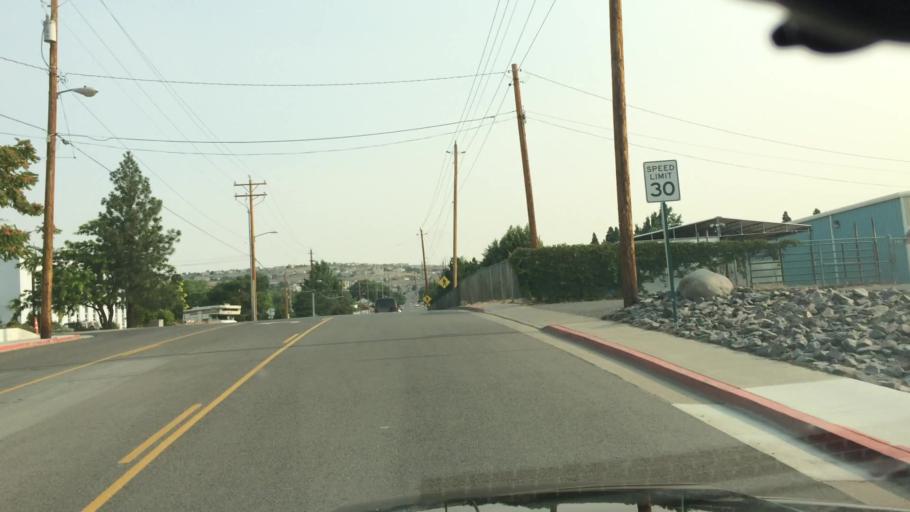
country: US
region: Nevada
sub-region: Washoe County
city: Reno
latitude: 39.5406
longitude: -119.8079
